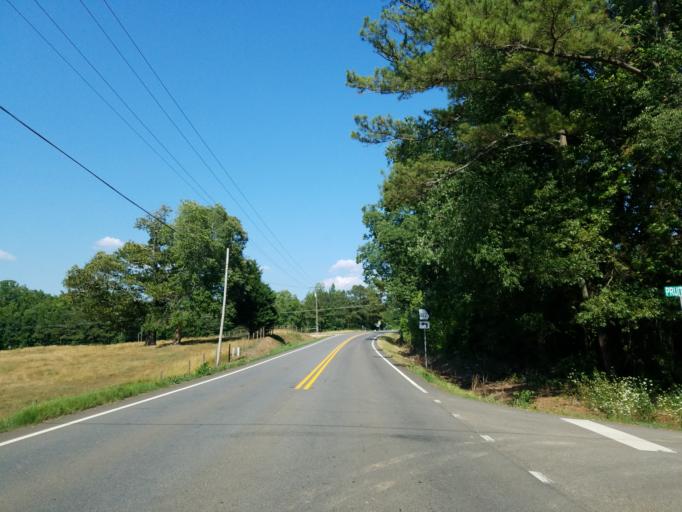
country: US
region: Georgia
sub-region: Fulton County
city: Milton
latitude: 34.2065
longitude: -84.2916
